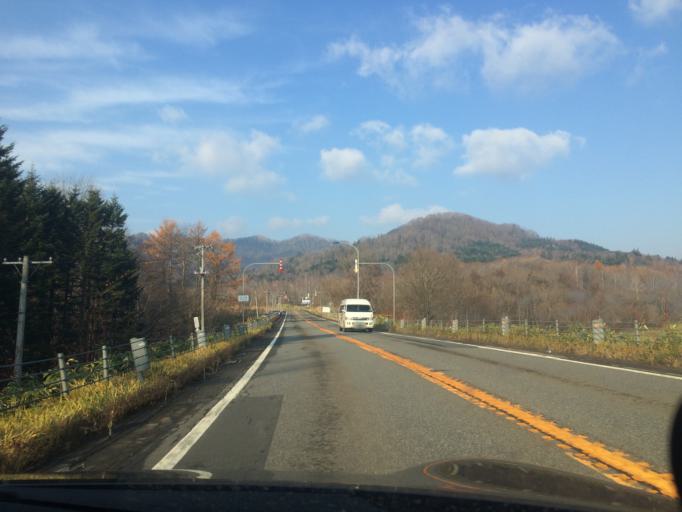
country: JP
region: Hokkaido
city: Shimo-furano
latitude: 42.8966
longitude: 142.4291
